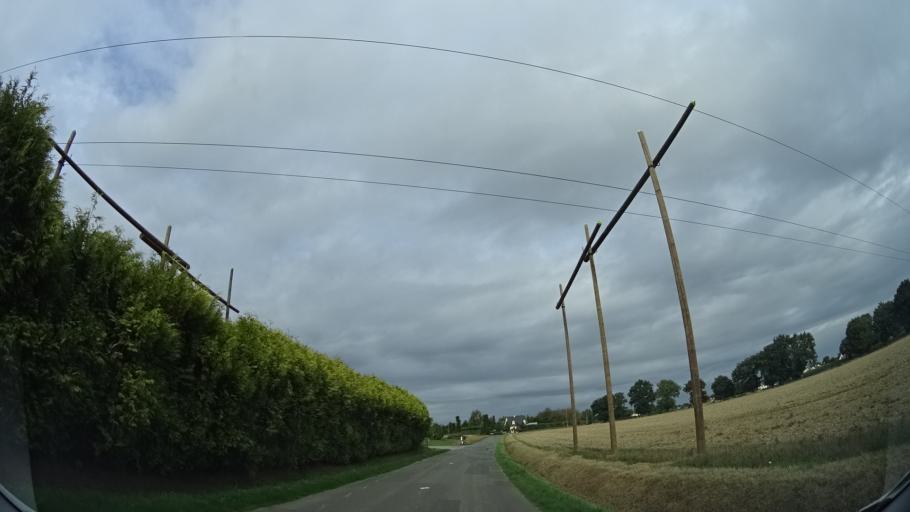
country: FR
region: Brittany
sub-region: Departement d'Ille-et-Vilaine
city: Hede-Bazouges
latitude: 48.2887
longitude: -1.8145
